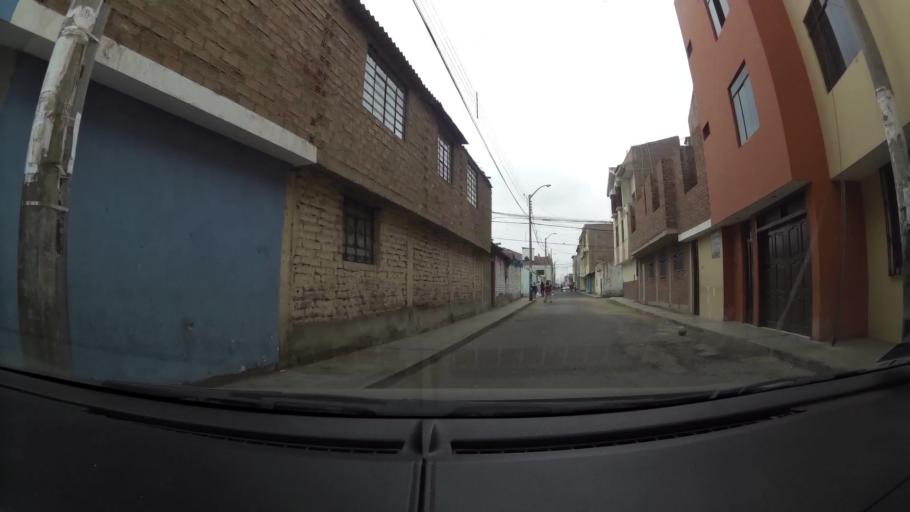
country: PE
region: La Libertad
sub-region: Provincia de Trujillo
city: Trujillo
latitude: -8.1061
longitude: -79.0401
